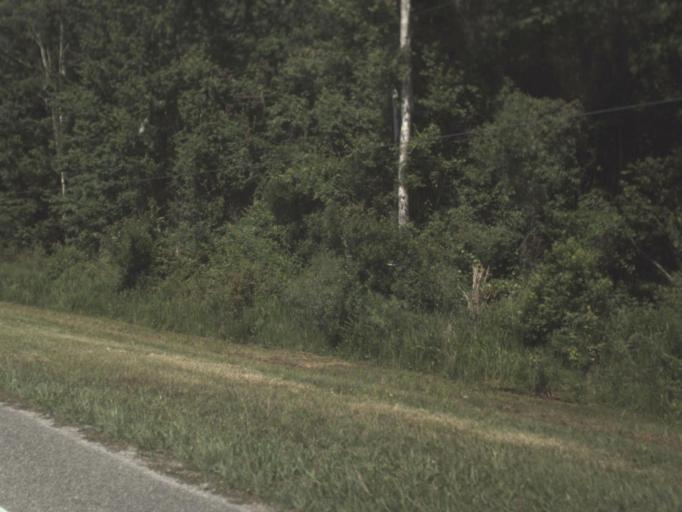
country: US
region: Florida
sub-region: Alachua County
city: Gainesville
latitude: 29.7078
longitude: -82.2739
